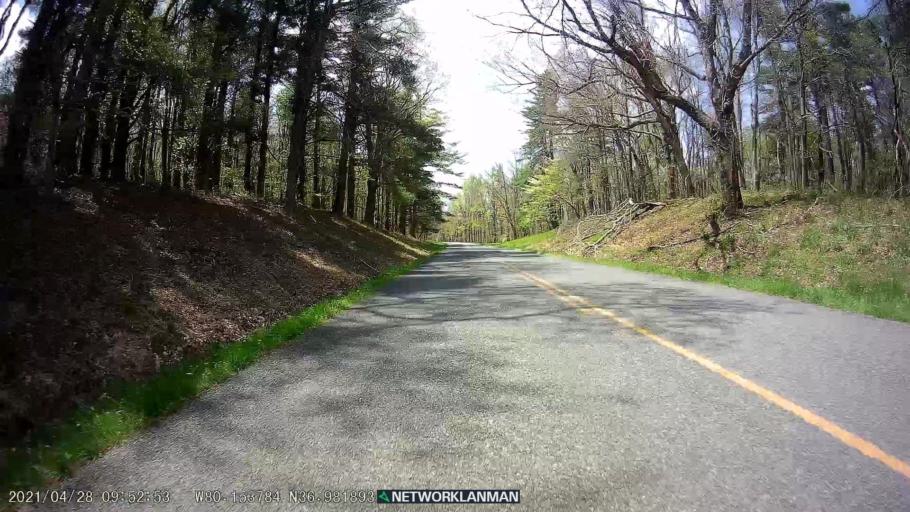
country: US
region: Virginia
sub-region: Franklin County
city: Ferrum
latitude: 36.9819
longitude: -80.1537
